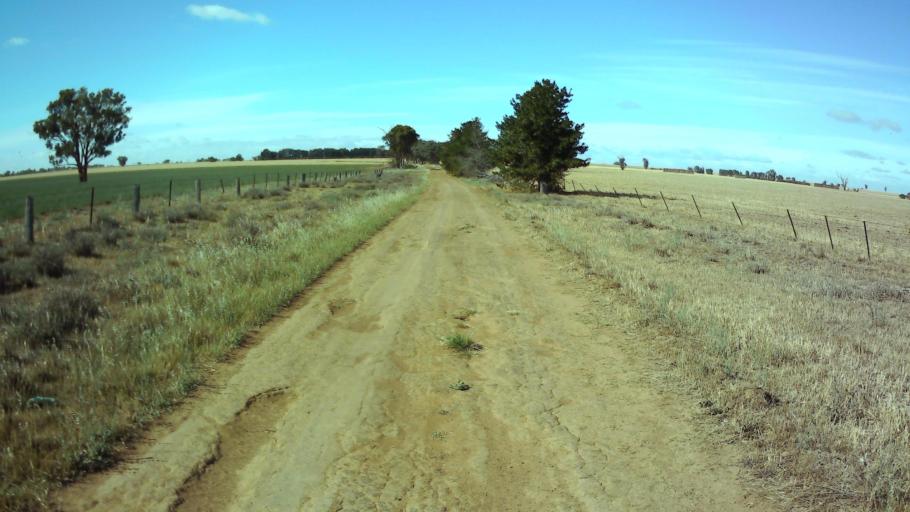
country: AU
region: New South Wales
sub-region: Weddin
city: Grenfell
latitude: -34.0504
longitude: 148.2691
